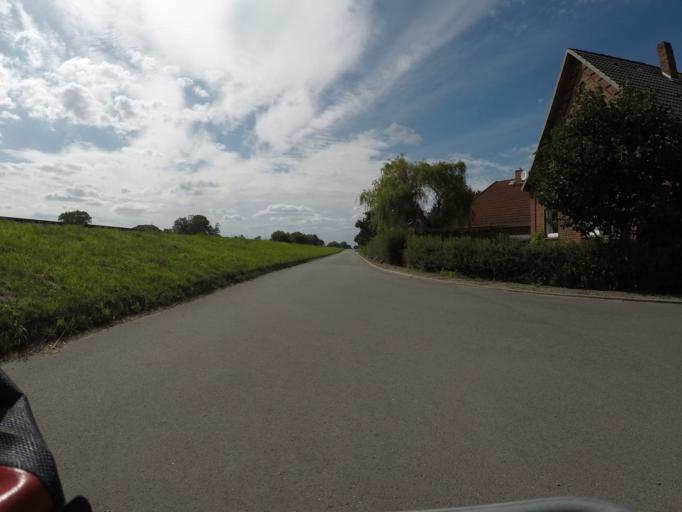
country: DE
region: Lower Saxony
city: Handorf
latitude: 53.3616
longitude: 10.3047
